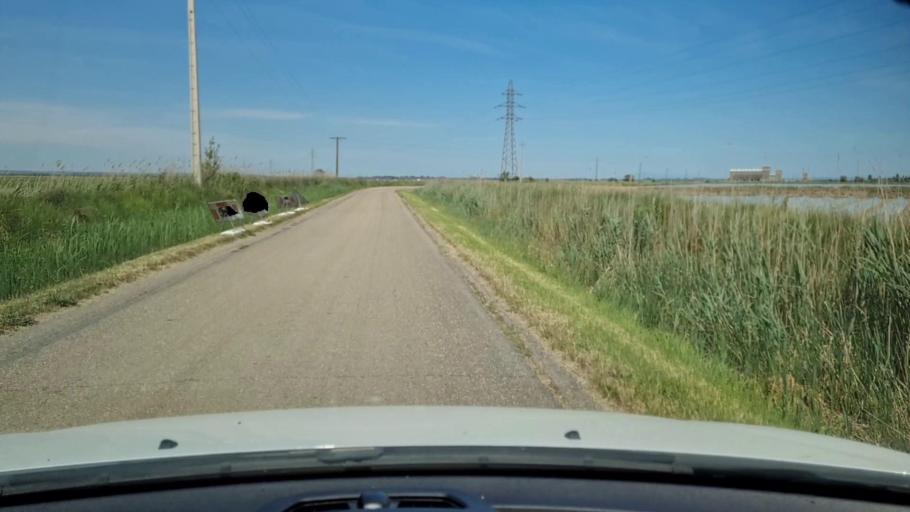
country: FR
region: Languedoc-Roussillon
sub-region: Departement du Gard
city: Saint-Gilles
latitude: 43.5784
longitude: 4.3985
